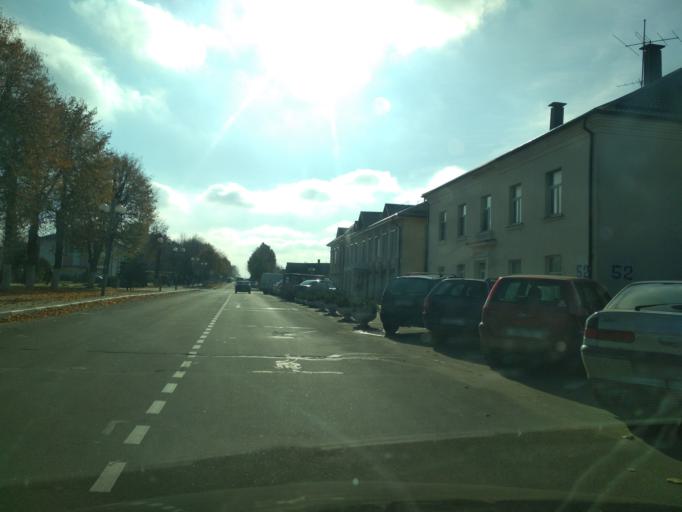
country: BY
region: Minsk
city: Mar''ina Horka
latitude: 53.5114
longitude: 28.1473
